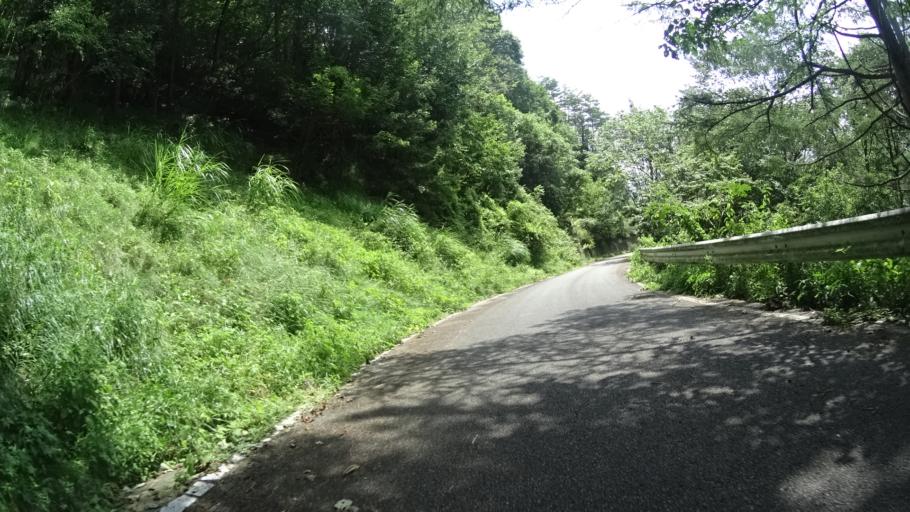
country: JP
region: Yamanashi
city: Nirasaki
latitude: 35.8830
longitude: 138.4895
